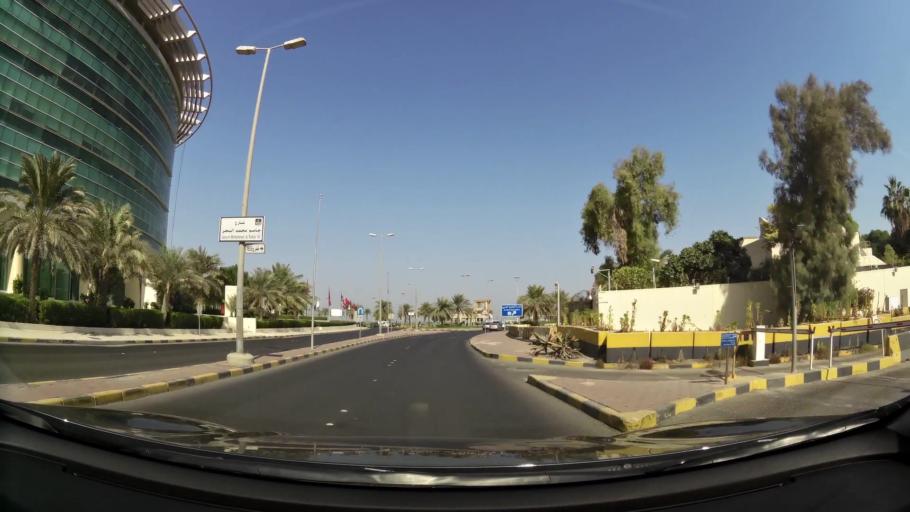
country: KW
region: Al Asimah
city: Kuwait City
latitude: 29.3895
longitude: 47.9943
